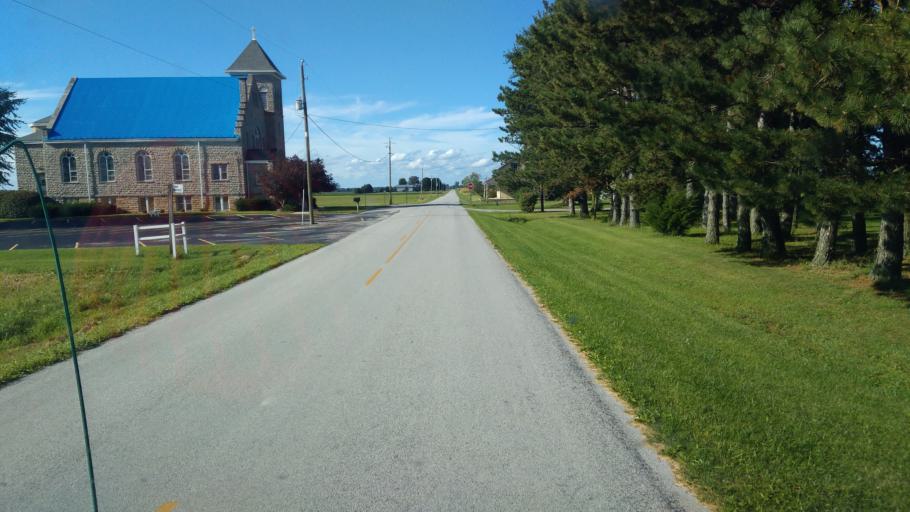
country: US
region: Ohio
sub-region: Hardin County
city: Kenton
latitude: 40.7461
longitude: -83.6906
